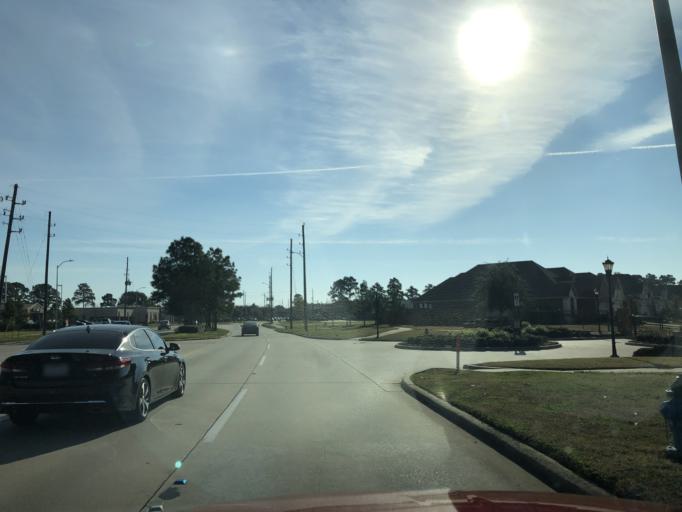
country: US
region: Texas
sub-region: Harris County
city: Tomball
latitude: 30.0346
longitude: -95.5583
